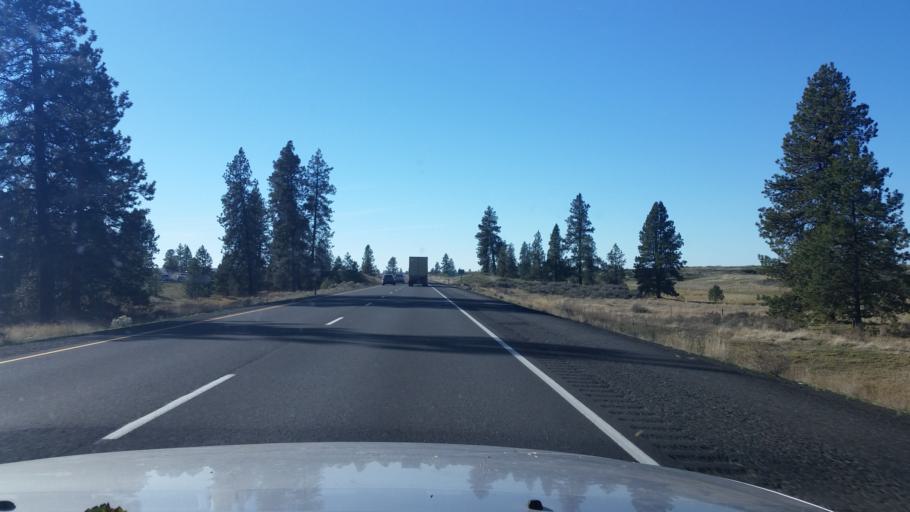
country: US
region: Washington
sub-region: Spokane County
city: Medical Lake
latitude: 47.4117
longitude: -117.8217
